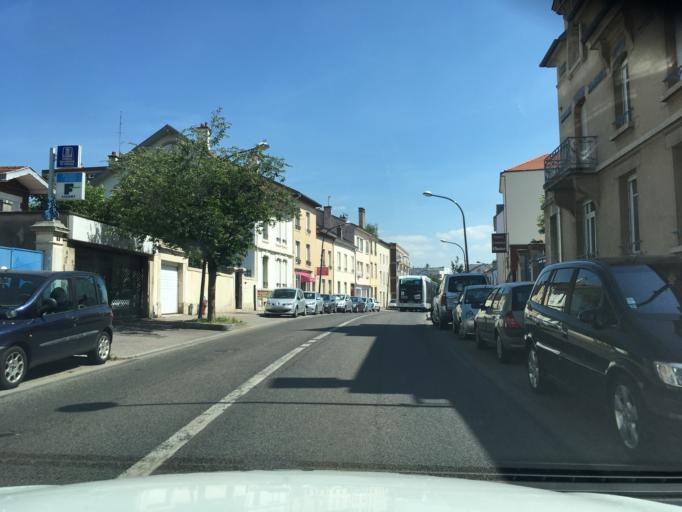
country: FR
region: Lorraine
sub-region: Departement de Meurthe-et-Moselle
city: Jarville-la-Malgrange
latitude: 48.6747
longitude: 6.2014
